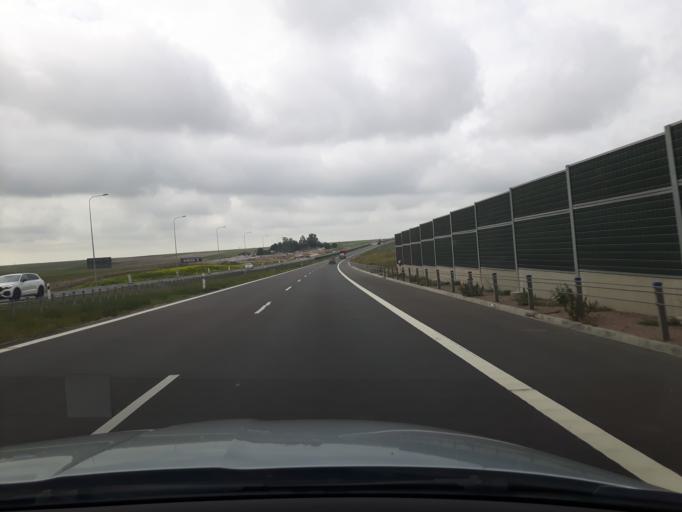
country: PL
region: Swietokrzyskie
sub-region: Powiat jedrzejowski
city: Sobkow
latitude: 50.7082
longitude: 20.4045
